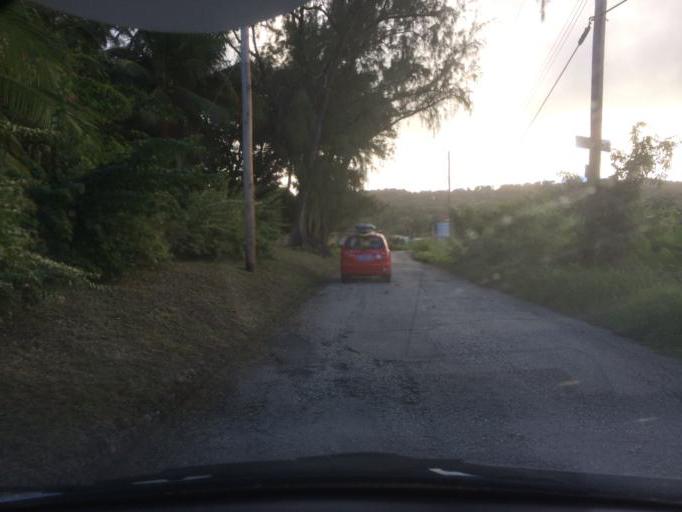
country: BB
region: Saint Joseph
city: Bathsheba
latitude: 13.2115
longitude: -59.5168
